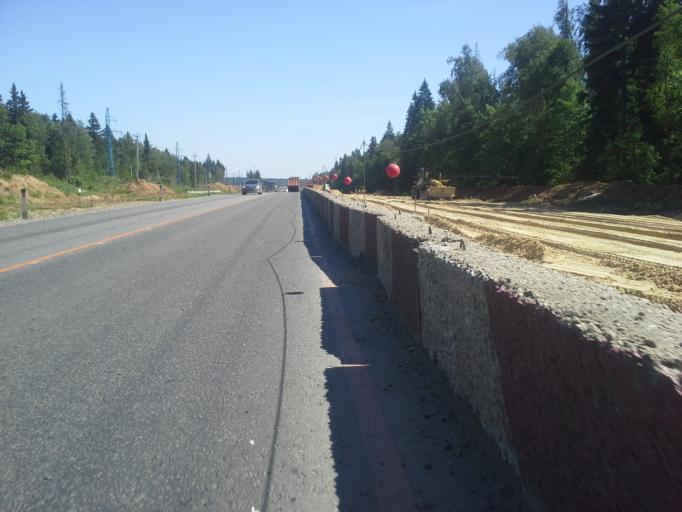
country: RU
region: Moskovskaya
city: Selyatino
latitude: 55.4862
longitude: 37.0452
